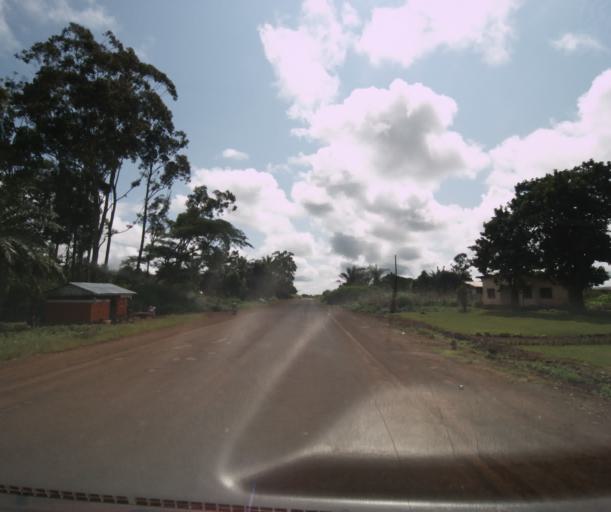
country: CM
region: West
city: Foumban
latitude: 5.6714
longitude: 10.7912
